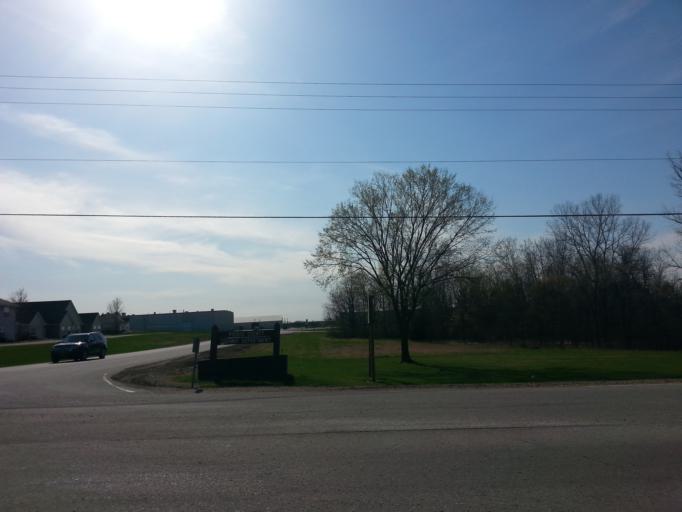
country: US
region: Wisconsin
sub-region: Pierce County
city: Ellsworth
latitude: 44.7418
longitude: -92.4870
